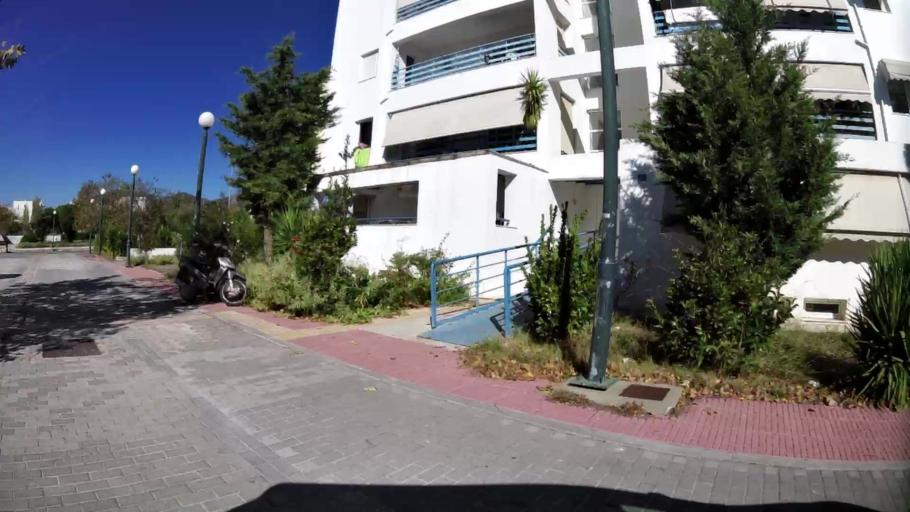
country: GR
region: Attica
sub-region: Nomarchia Anatolikis Attikis
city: Thrakomakedones
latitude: 38.1103
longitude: 23.7696
